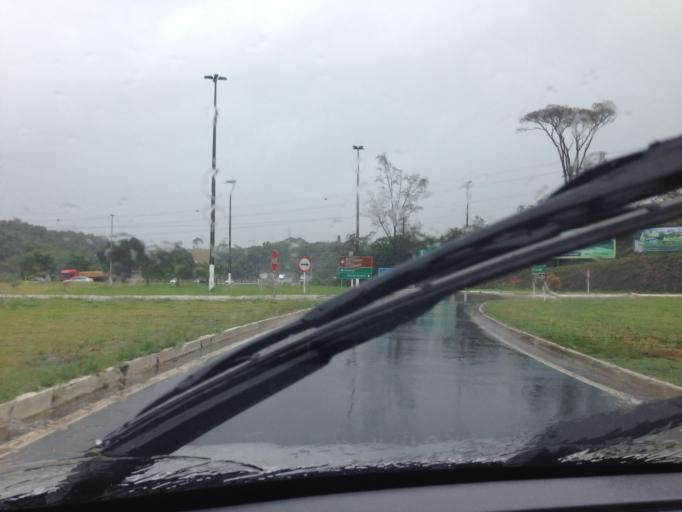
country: BR
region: Espirito Santo
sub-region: Guarapari
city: Guarapari
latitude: -20.6273
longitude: -40.5276
